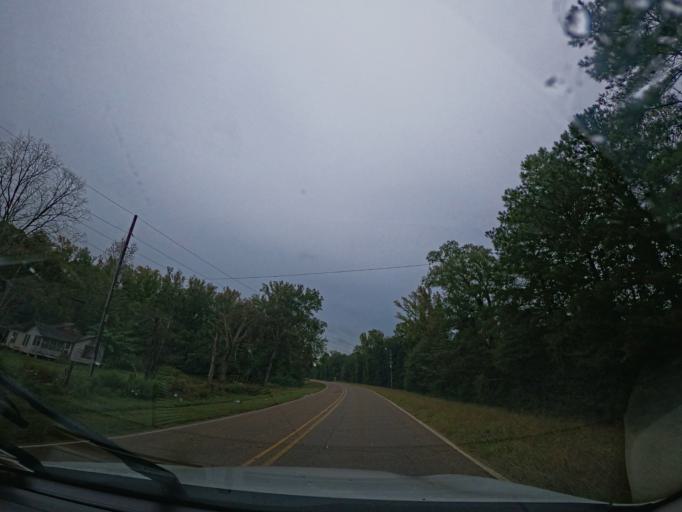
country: US
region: Louisiana
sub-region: Bienville Parish
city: Arcadia
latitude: 32.5519
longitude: -93.0529
